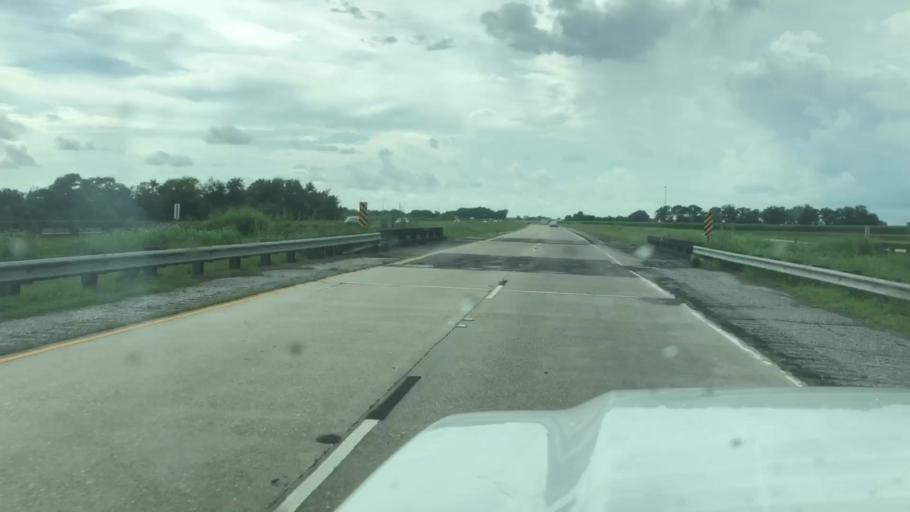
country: US
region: Louisiana
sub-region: Saint Mary Parish
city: Baldwin
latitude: 29.8571
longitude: -91.6116
